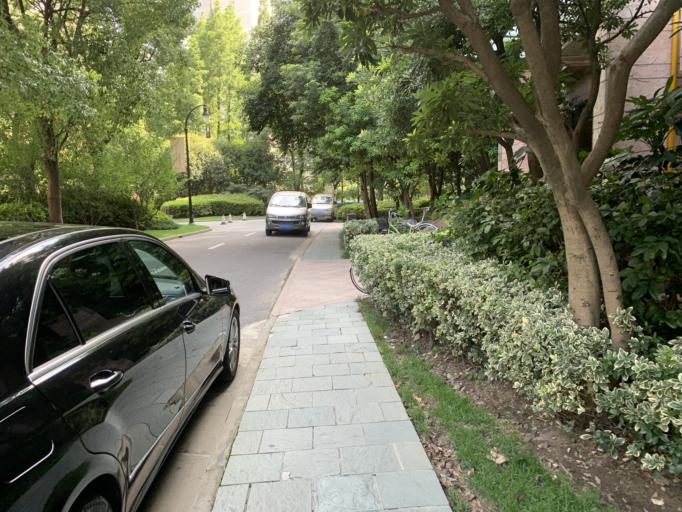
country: CN
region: Shanghai Shi
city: Pudong
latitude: 31.2323
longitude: 121.5064
